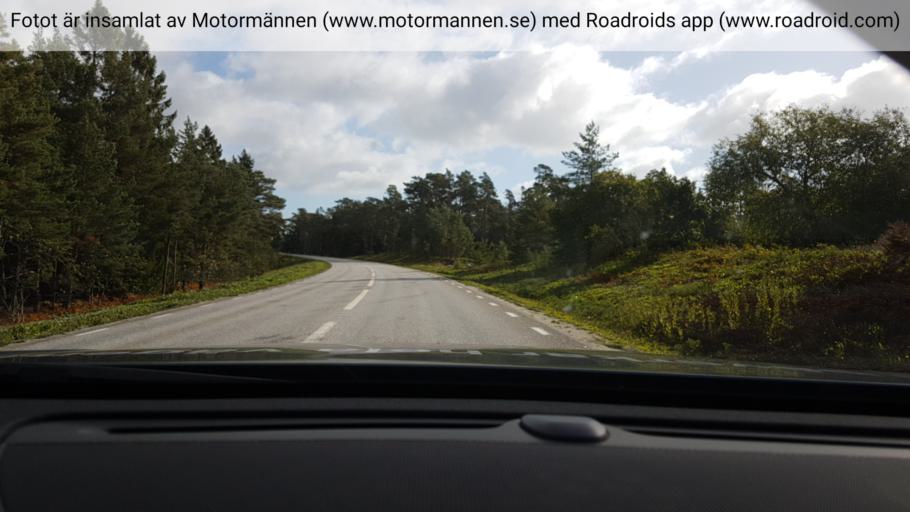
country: SE
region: Gotland
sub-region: Gotland
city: Slite
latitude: 57.8396
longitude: 18.9481
